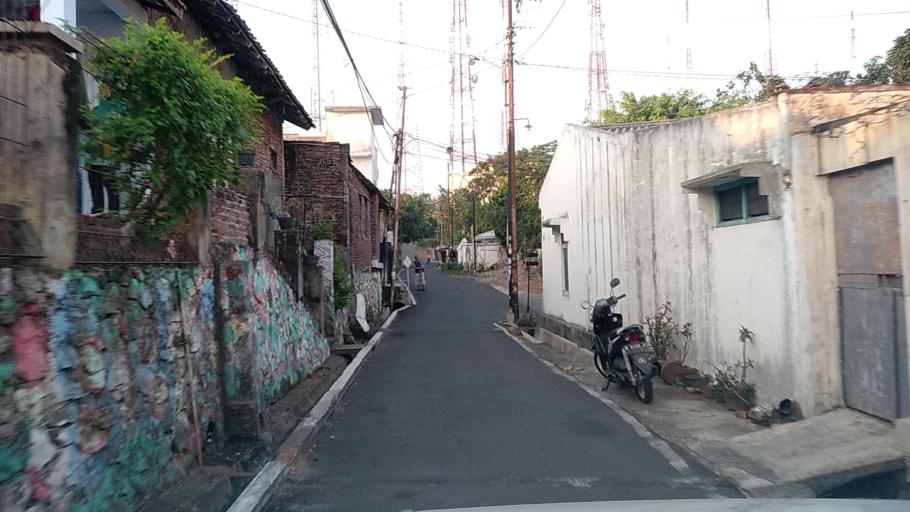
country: ID
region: Central Java
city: Semarang
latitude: -7.0471
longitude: 110.4229
